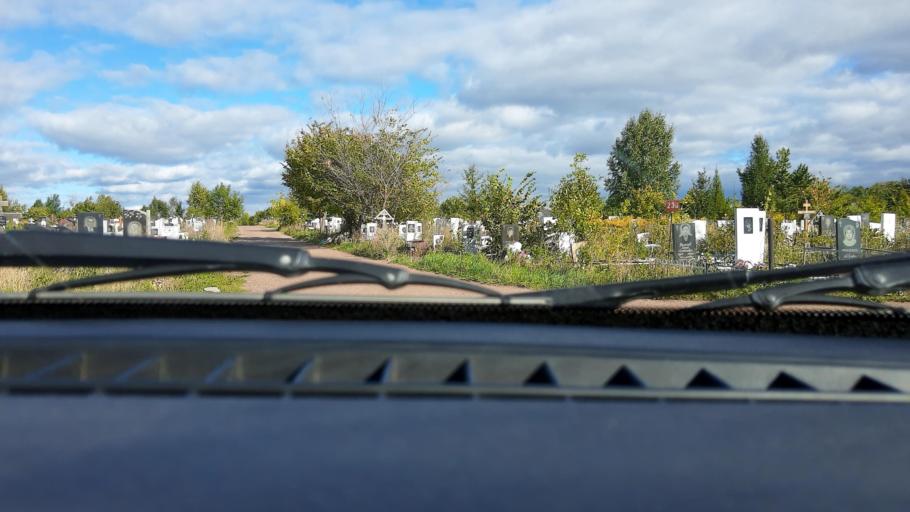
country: RU
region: Bashkortostan
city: Mikhaylovka
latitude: 54.8156
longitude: 55.8622
